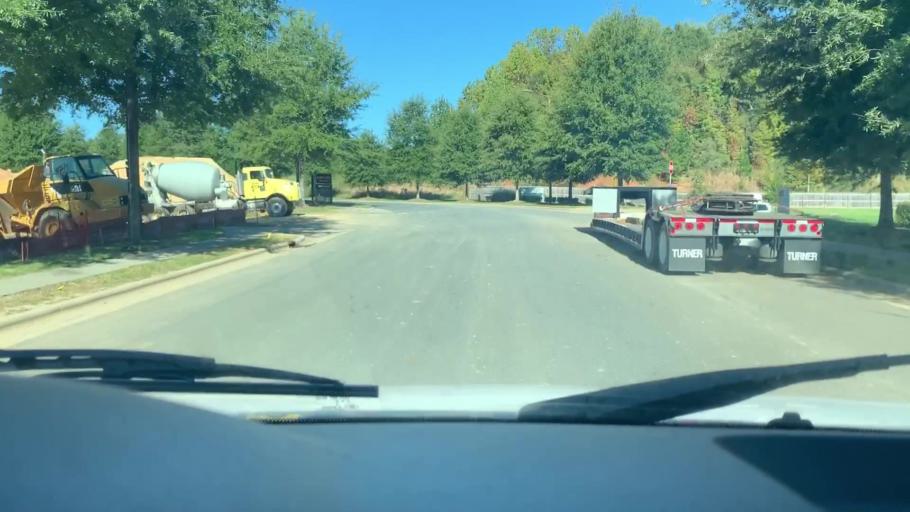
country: US
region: North Carolina
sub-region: Gaston County
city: Belmont
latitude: 35.2468
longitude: -80.9818
